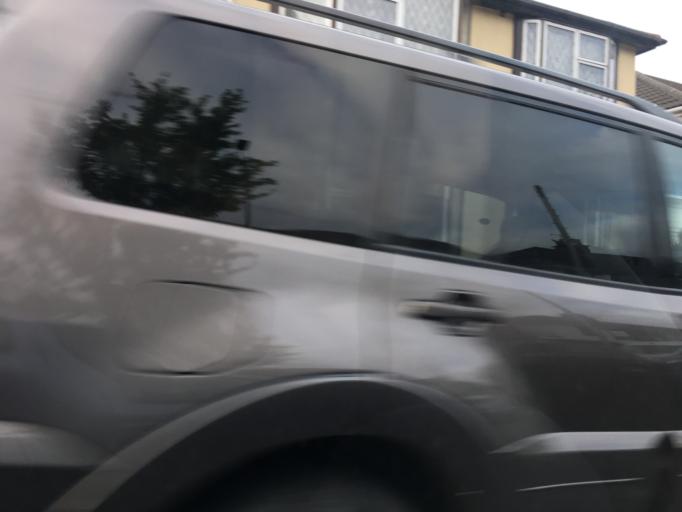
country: GB
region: England
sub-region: City of Leicester
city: Leicester
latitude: 52.6288
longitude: -1.1063
